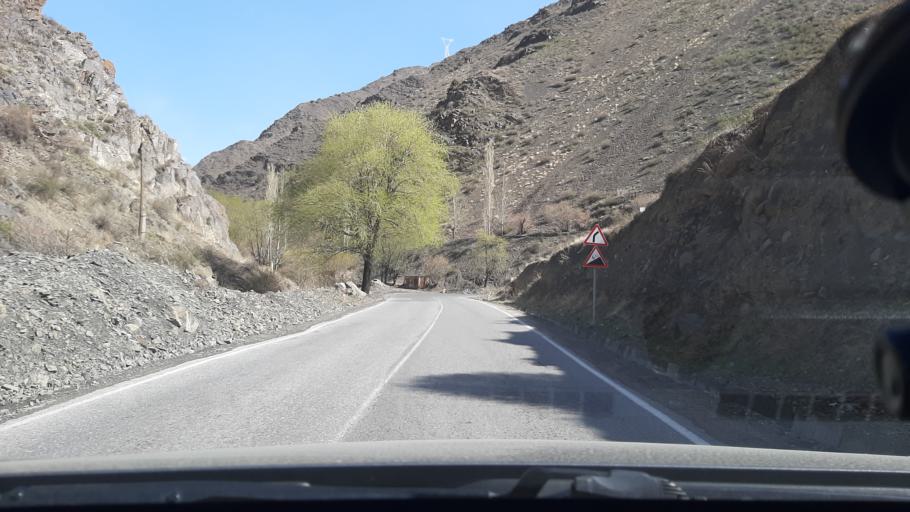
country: TJ
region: Viloyati Sughd
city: Ayni
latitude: 39.4592
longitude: 68.5462
